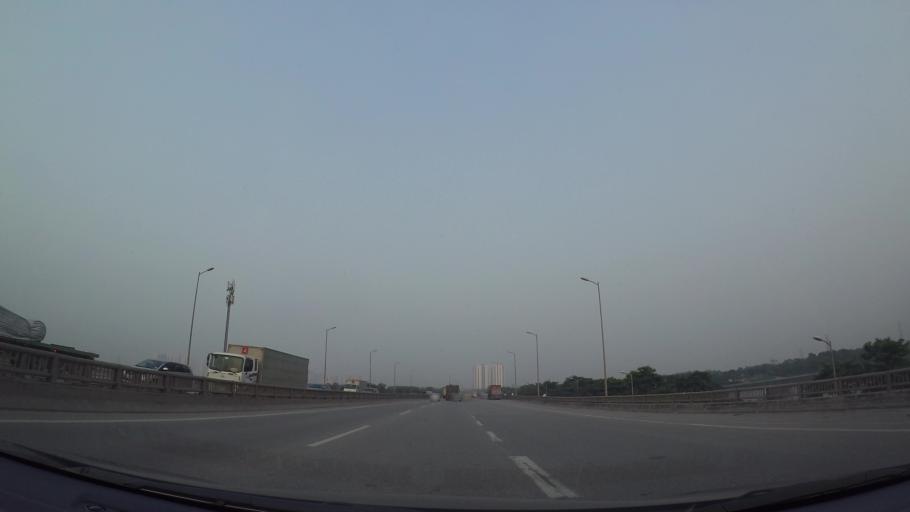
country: VN
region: Ha Noi
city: Van Dien
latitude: 20.9657
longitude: 105.8512
